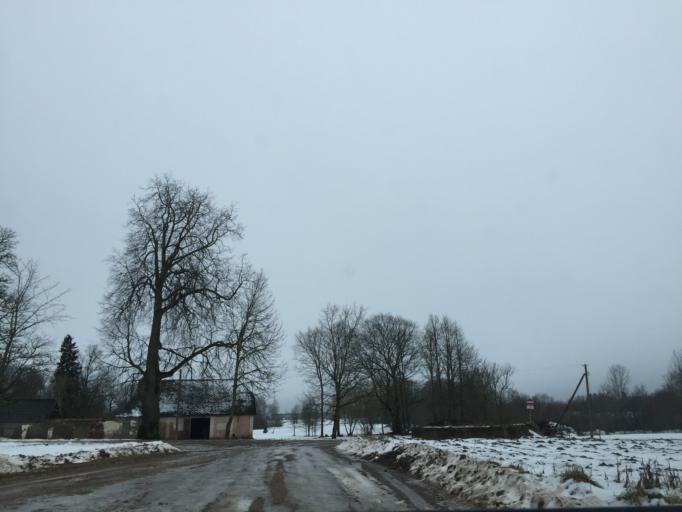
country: LV
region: Krimulda
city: Ragana
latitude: 57.1703
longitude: 24.7174
